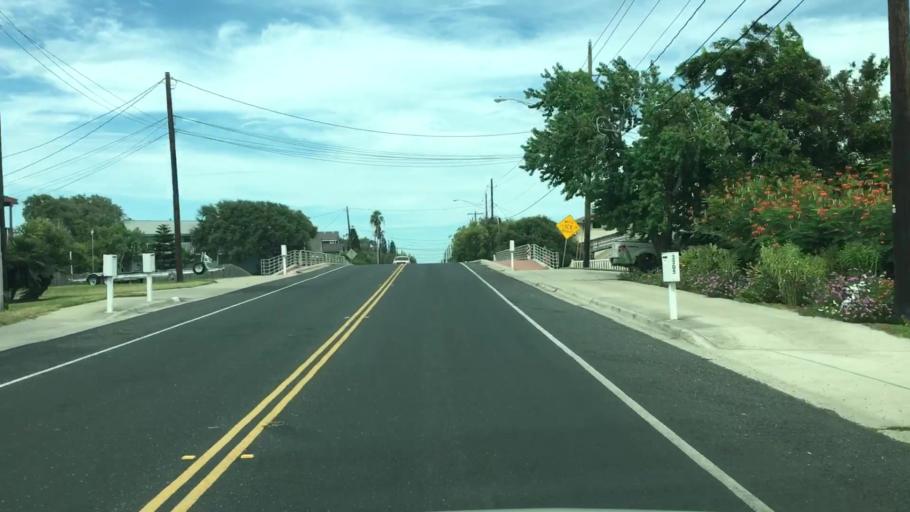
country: US
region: Texas
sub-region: Nueces County
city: Corpus Christi
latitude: 27.6272
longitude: -97.2928
